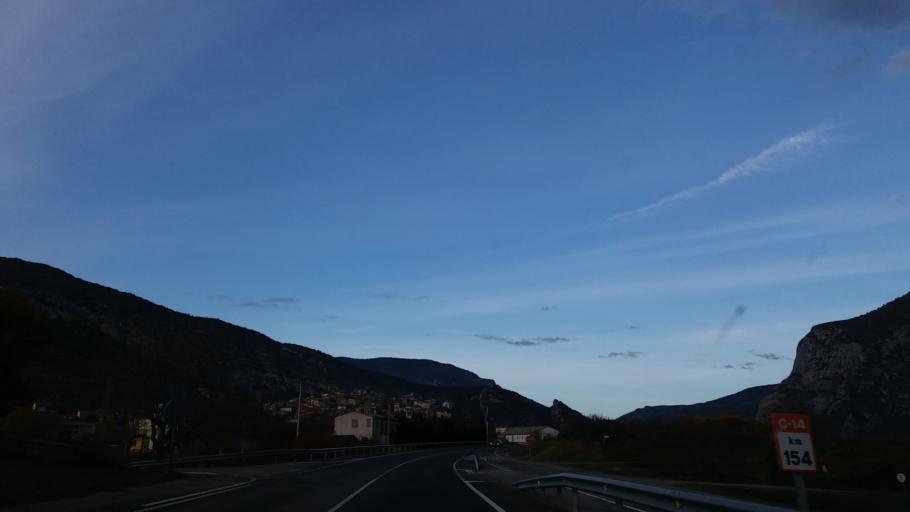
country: ES
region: Catalonia
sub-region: Provincia de Lleida
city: Coll de Nargo
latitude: 42.1677
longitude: 1.3174
